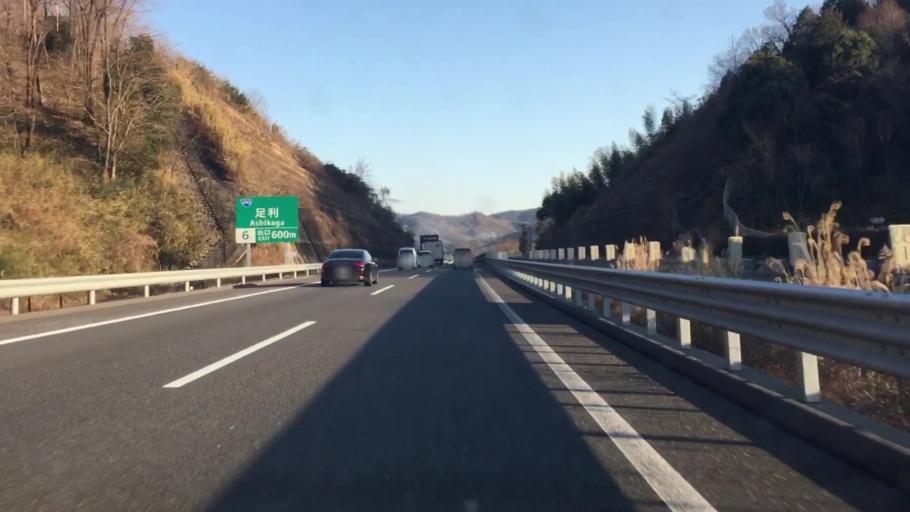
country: JP
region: Tochigi
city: Ashikaga
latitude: 36.3656
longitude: 139.4748
